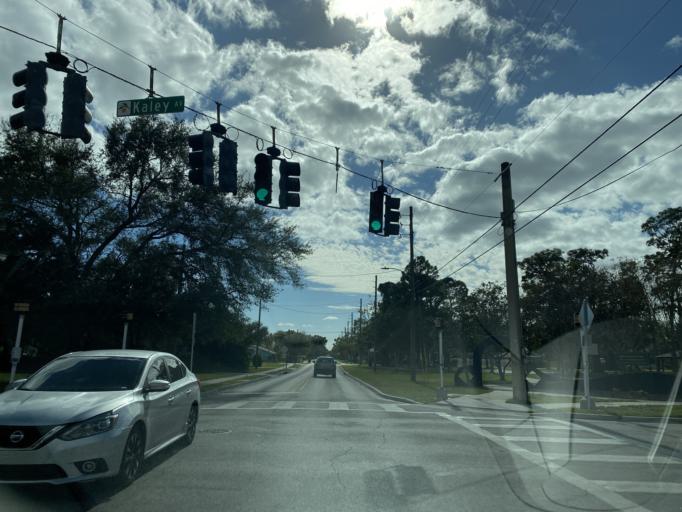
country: US
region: Florida
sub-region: Orange County
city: Orlando
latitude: 28.5202
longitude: -81.3929
